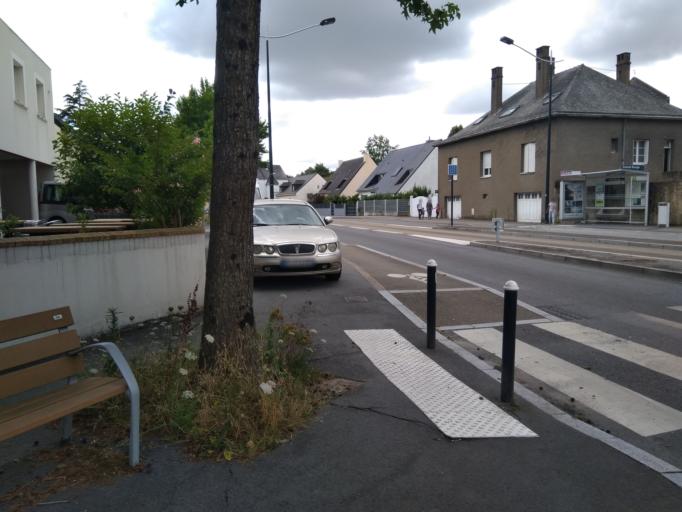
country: FR
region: Pays de la Loire
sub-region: Departement de la Loire-Atlantique
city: Sainte-Luce-sur-Loire
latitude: 47.2440
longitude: -1.5047
